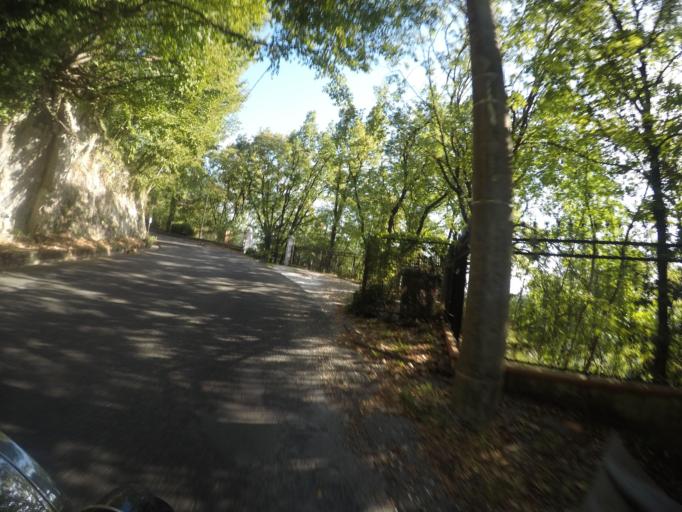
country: IT
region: Tuscany
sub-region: Provincia di Massa-Carrara
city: Massa
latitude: 44.0686
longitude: 10.1177
